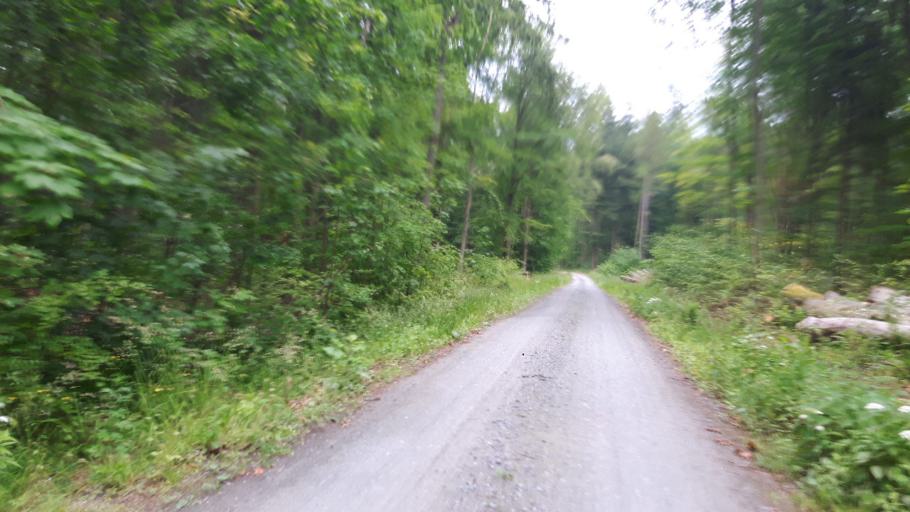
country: PL
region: Warmian-Masurian Voivodeship
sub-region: Powiat elblaski
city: Tolkmicko
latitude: 54.3324
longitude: 19.5887
